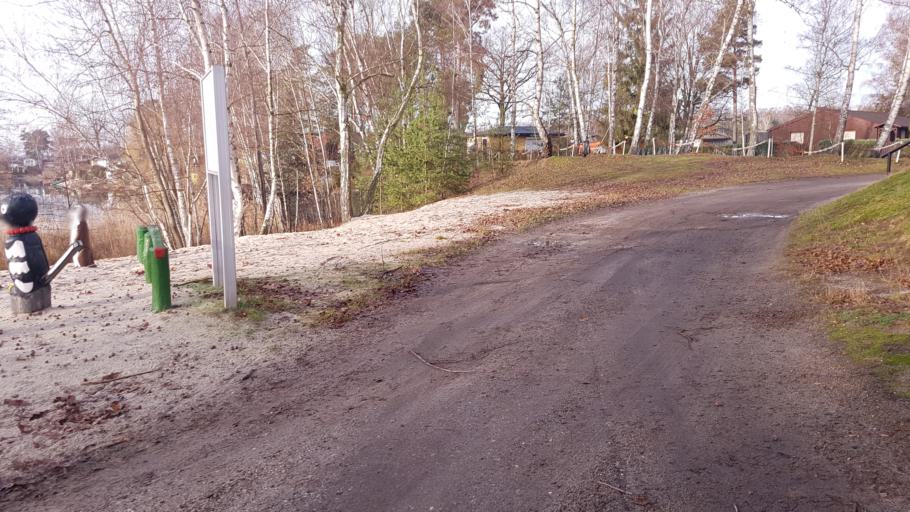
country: DE
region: Brandenburg
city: Ruckersdorf
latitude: 51.5934
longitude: 13.5643
